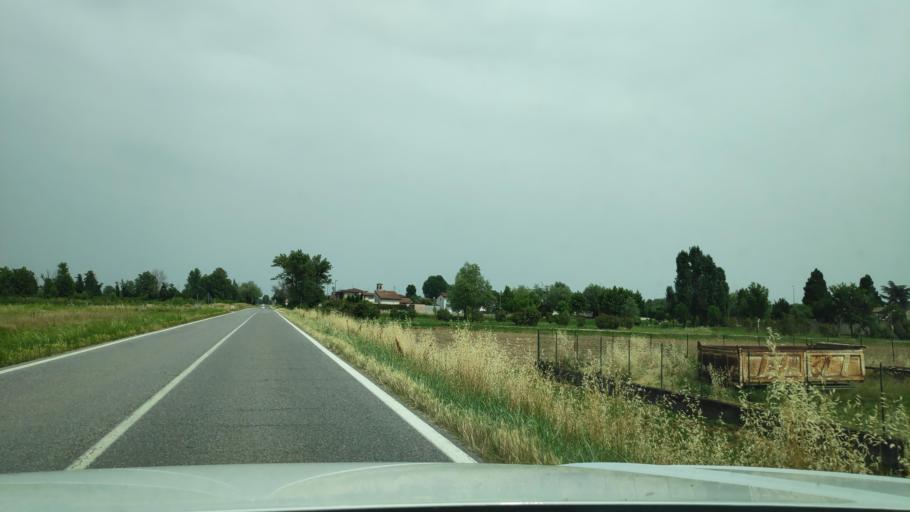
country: IT
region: Lombardy
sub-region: Provincia di Cremona
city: Casaletto di Sopra
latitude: 45.4140
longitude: 9.7981
